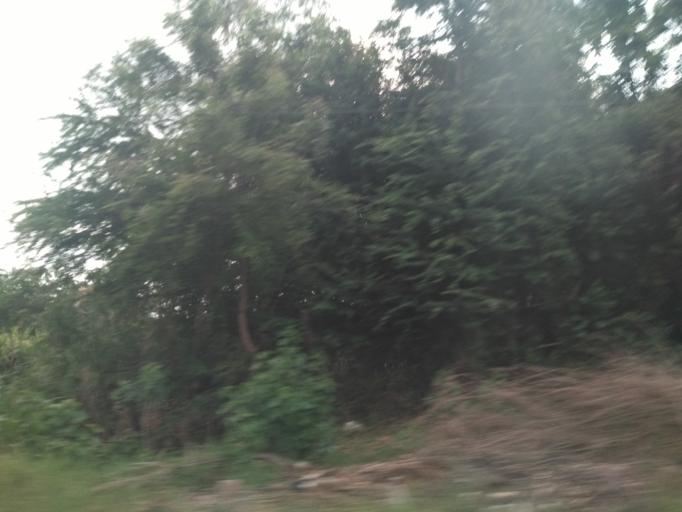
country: TZ
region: Dar es Salaam
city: Magomeni
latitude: -6.7469
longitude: 39.2360
